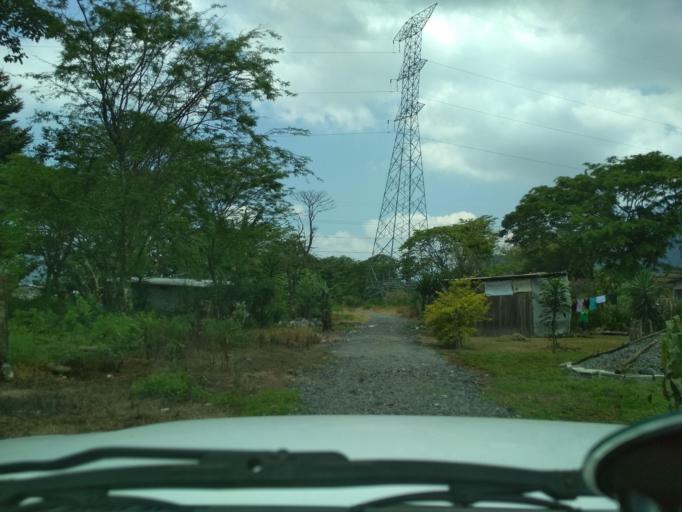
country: MX
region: Veracruz
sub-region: Ixtaczoquitlan
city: Buenavista
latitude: 18.8869
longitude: -97.0629
